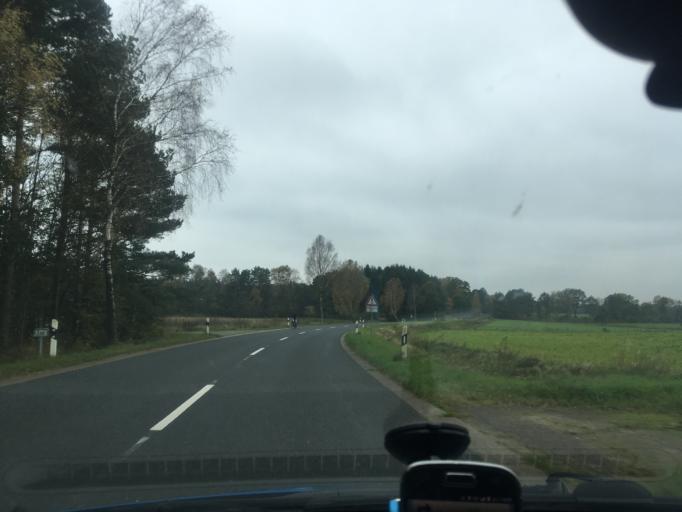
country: DE
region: Lower Saxony
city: Soderstorf
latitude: 53.1060
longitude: 10.0798
